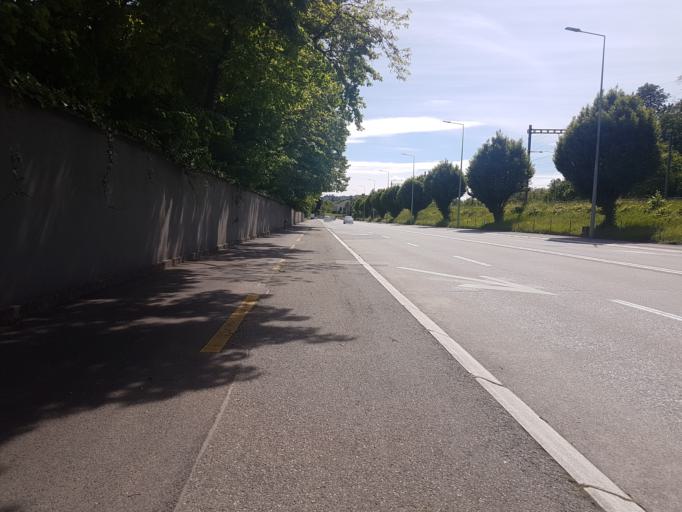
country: CH
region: Geneva
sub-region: Geneva
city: Bellevue
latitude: 46.2609
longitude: 6.1591
